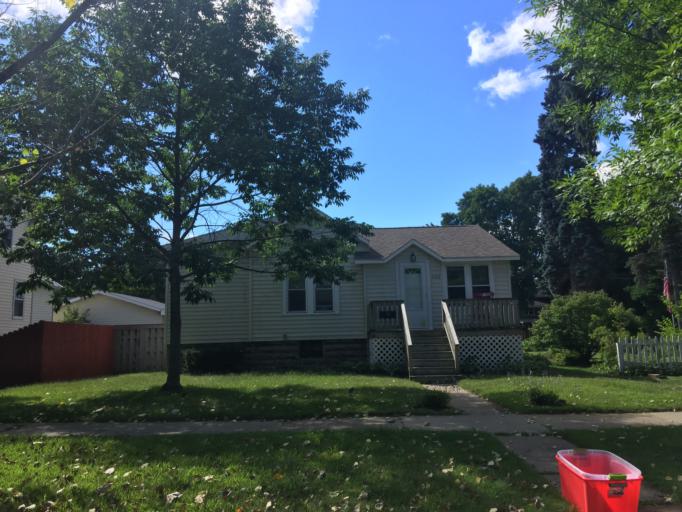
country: US
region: Wisconsin
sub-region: Oconto County
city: Oconto
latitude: 44.8882
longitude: -87.8628
